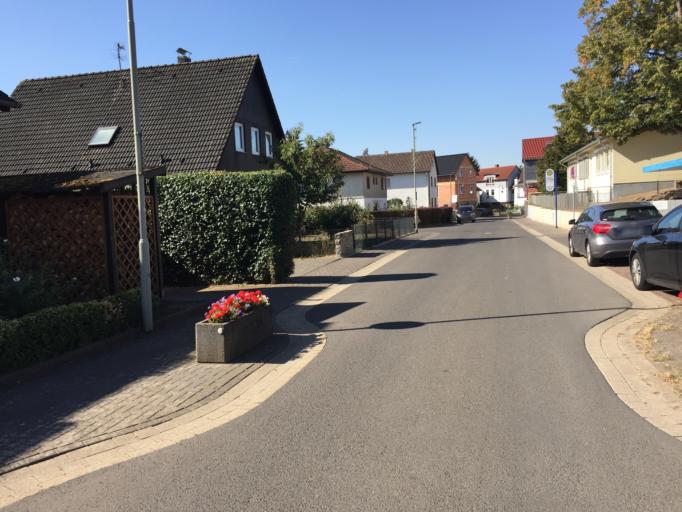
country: DE
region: Hesse
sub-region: Regierungsbezirk Darmstadt
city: Nidda
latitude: 50.4269
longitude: 8.9453
